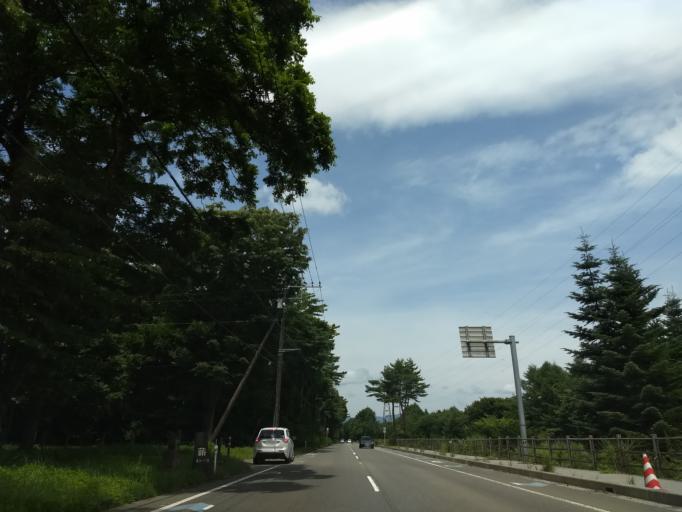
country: JP
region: Yamanashi
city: Fujikawaguchiko
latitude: 35.4381
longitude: 138.8370
